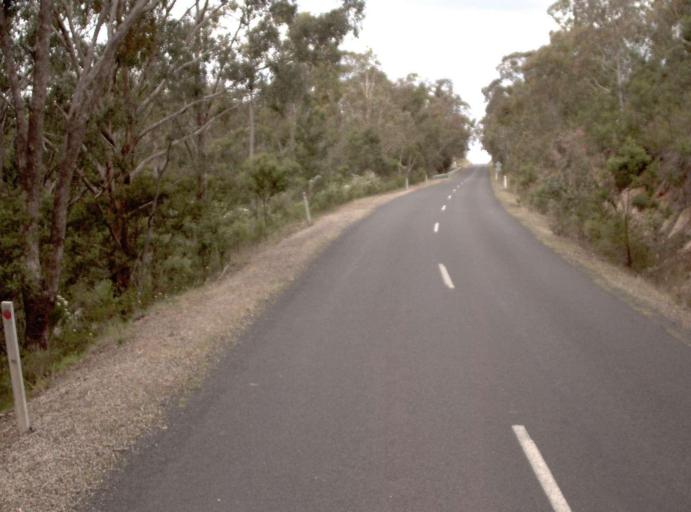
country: AU
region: Victoria
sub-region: East Gippsland
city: Bairnsdale
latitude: -37.4742
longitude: 147.2154
